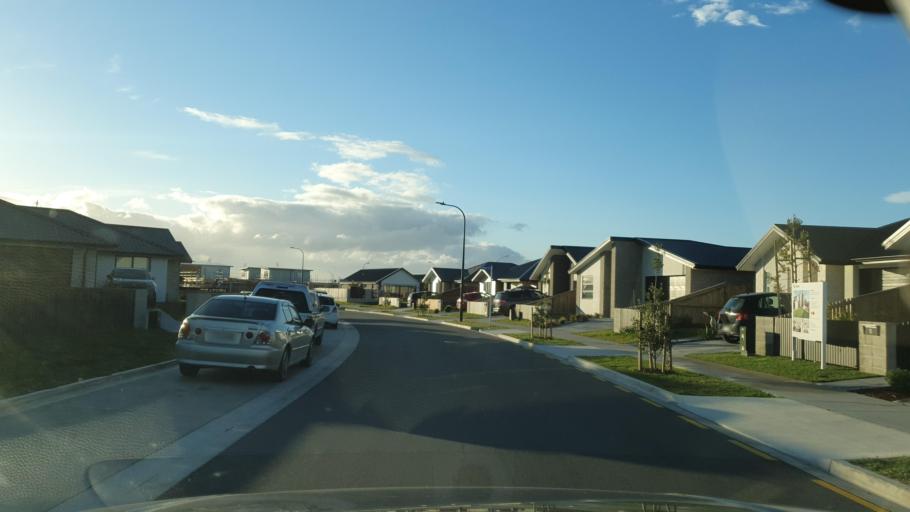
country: NZ
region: Bay of Plenty
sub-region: Western Bay of Plenty District
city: Maketu
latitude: -37.7287
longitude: 176.3377
